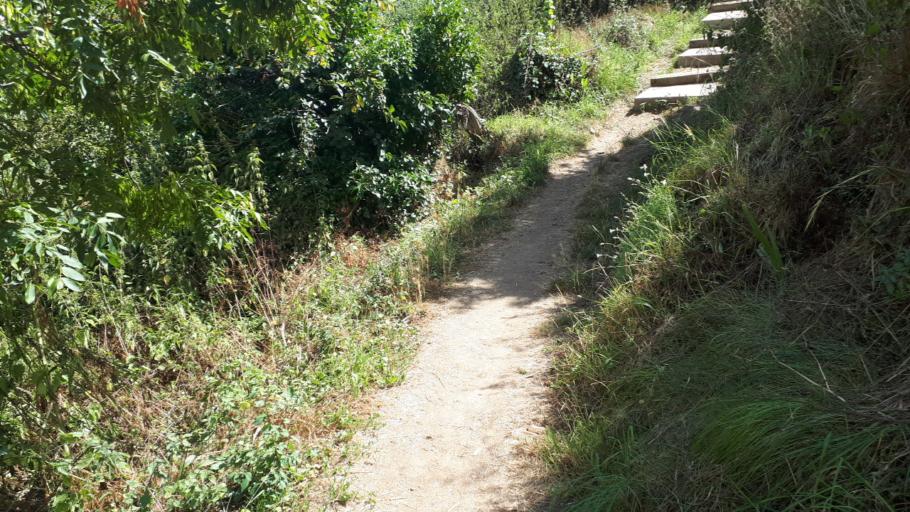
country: FR
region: Brittany
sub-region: Departement des Cotes-d'Armor
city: Etables-sur-Mer
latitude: 48.6347
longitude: -2.8237
